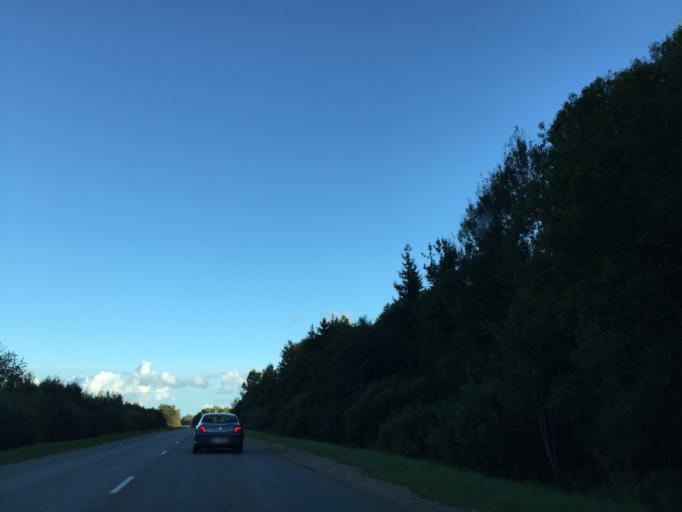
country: LV
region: Kuldigas Rajons
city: Kuldiga
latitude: 56.9505
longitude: 22.0129
